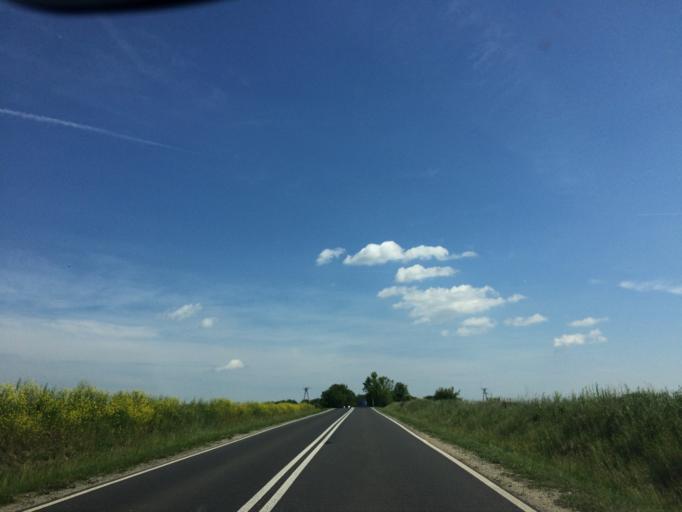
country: PL
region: Lower Silesian Voivodeship
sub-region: Powiat swidnicki
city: Swidnica
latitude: 50.8188
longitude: 16.4984
